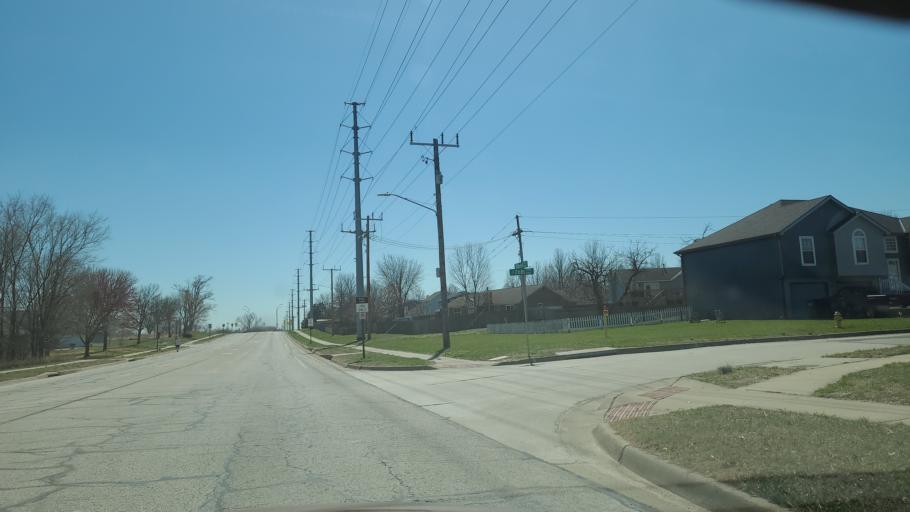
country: US
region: Kansas
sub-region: Douglas County
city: Lawrence
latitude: 38.9364
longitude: -95.2049
